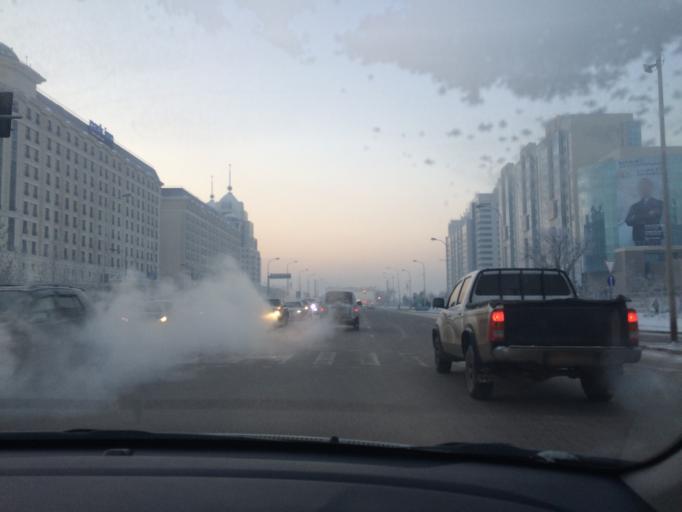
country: KZ
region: Astana Qalasy
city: Astana
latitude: 51.1632
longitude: 71.4097
